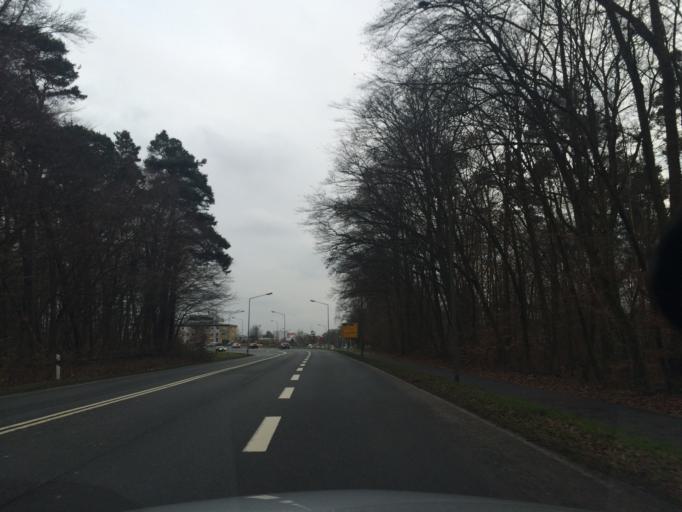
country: DE
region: Hesse
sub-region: Regierungsbezirk Darmstadt
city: Neu Isenburg
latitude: 50.0376
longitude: 8.6953
